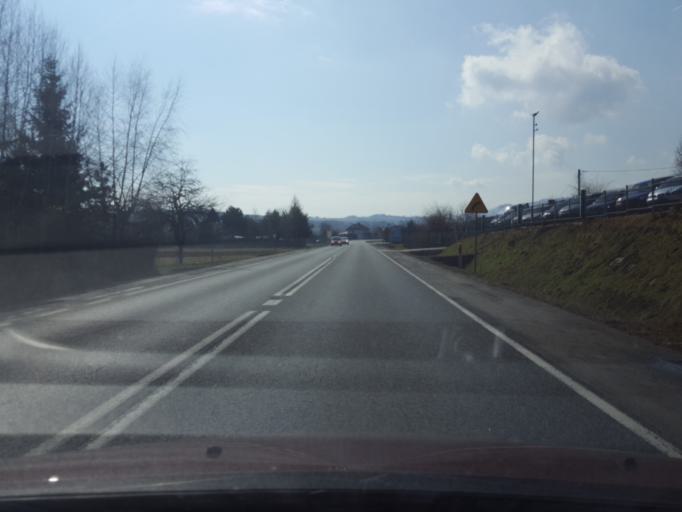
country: PL
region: Lesser Poland Voivodeship
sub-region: Powiat nowosadecki
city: Lososina Dolna
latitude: 49.7594
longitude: 20.6348
